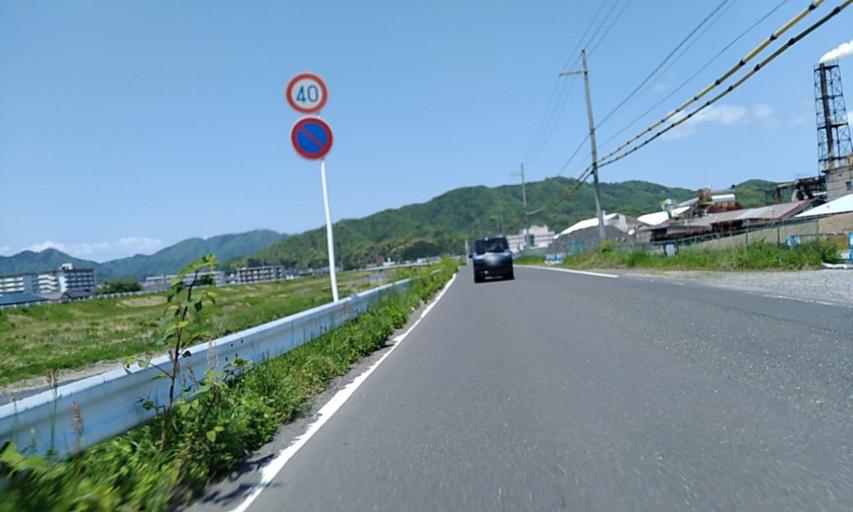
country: JP
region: Kyoto
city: Maizuru
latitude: 35.4390
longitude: 135.3362
